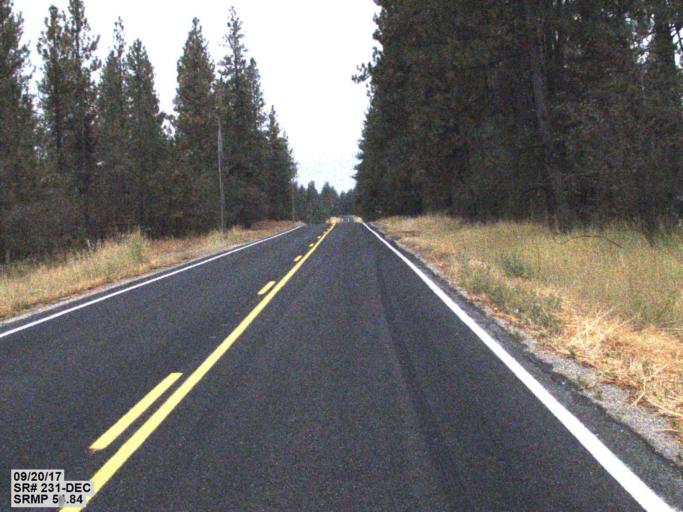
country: US
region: Washington
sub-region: Spokane County
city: Deer Park
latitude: 47.9586
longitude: -117.7508
